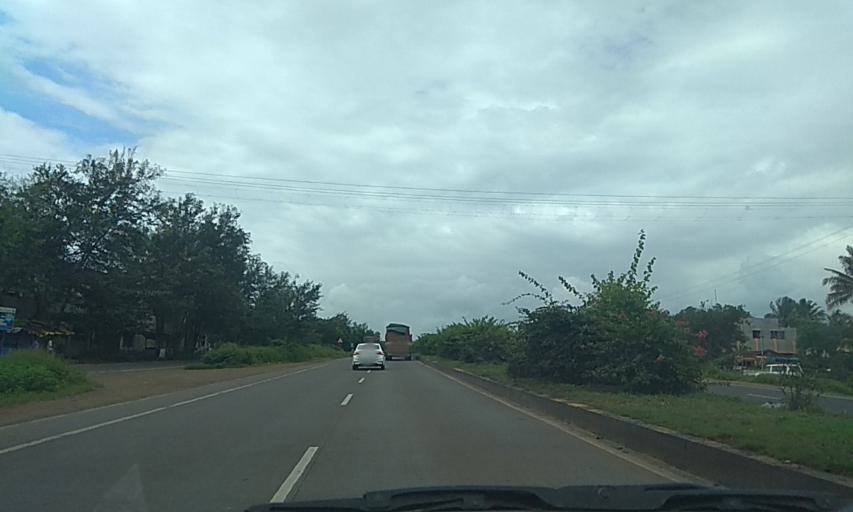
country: IN
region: Maharashtra
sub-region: Kolhapur
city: Kagal
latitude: 16.5886
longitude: 74.3085
